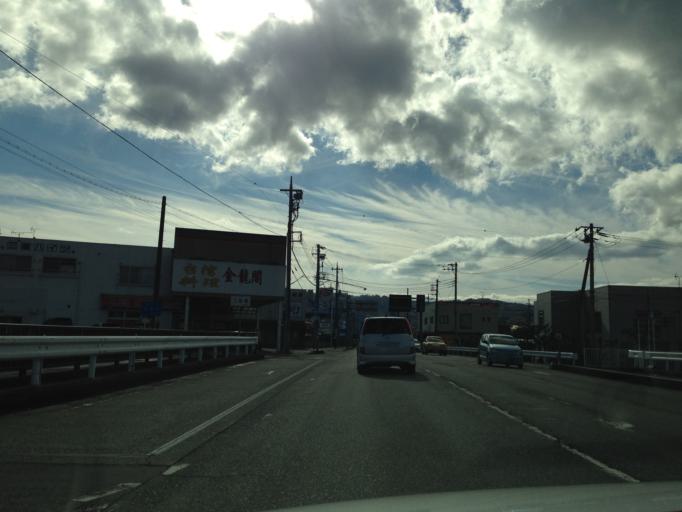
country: JP
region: Shizuoka
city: Mishima
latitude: 35.0102
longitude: 138.9432
